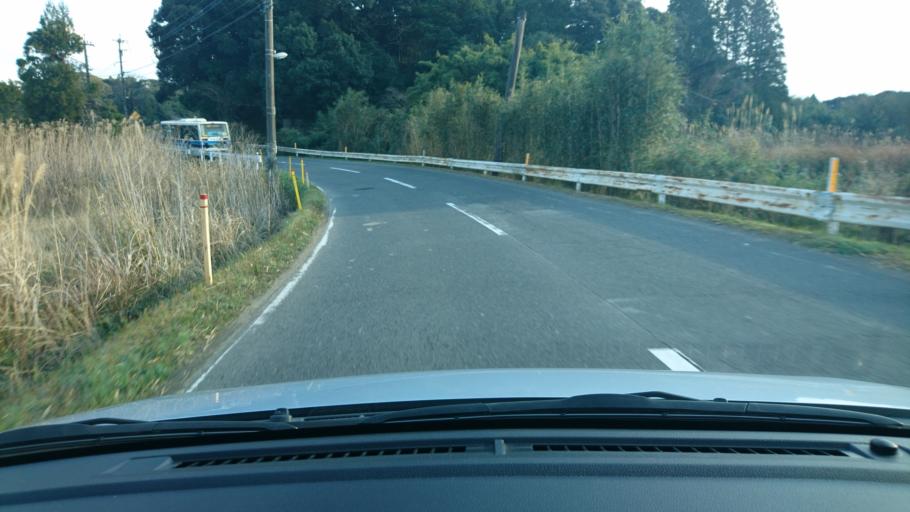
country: JP
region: Miyazaki
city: Miyazaki-shi
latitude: 31.8703
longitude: 131.4035
